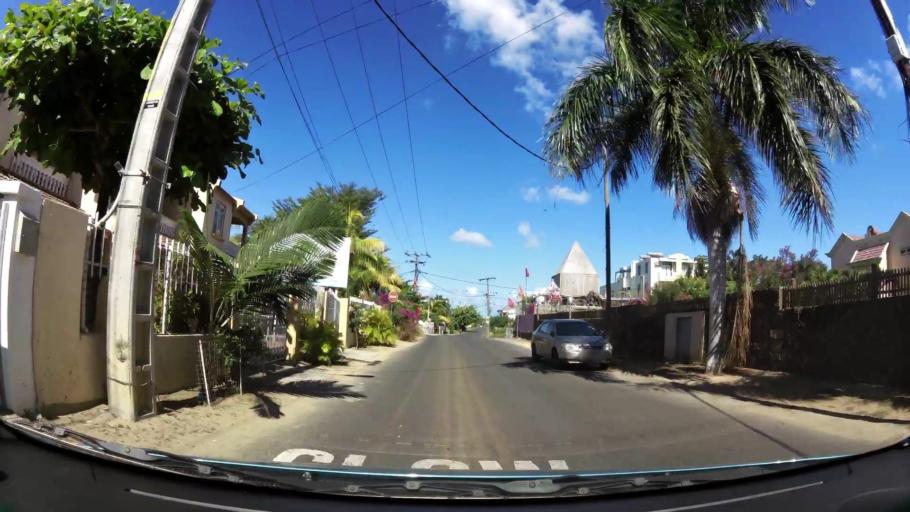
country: MU
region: Black River
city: Flic en Flac
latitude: -20.2804
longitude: 57.3686
